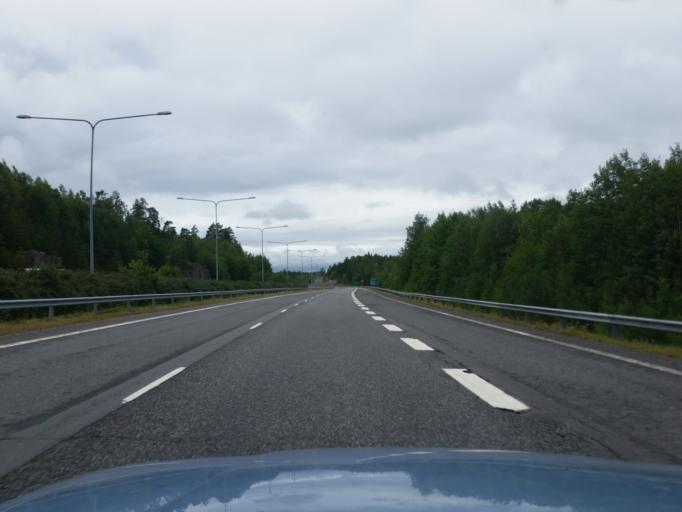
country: FI
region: Varsinais-Suomi
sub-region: Turku
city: Piikkioe
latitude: 60.4409
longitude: 22.4808
